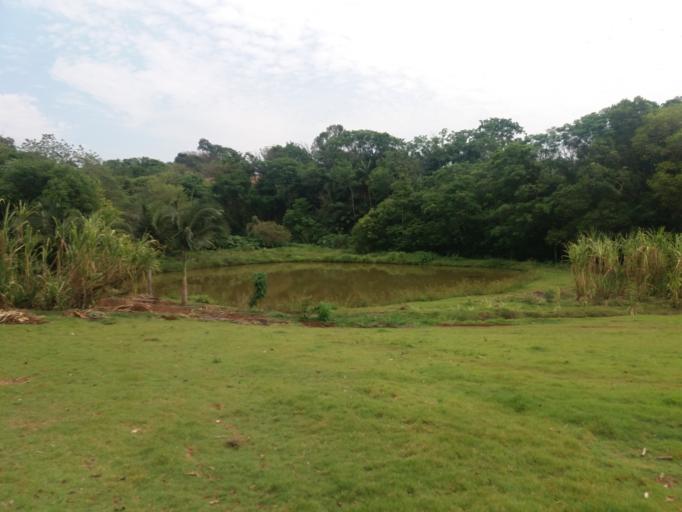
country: BR
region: Parana
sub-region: Londrina
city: Londrina
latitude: -23.5395
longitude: -51.1033
